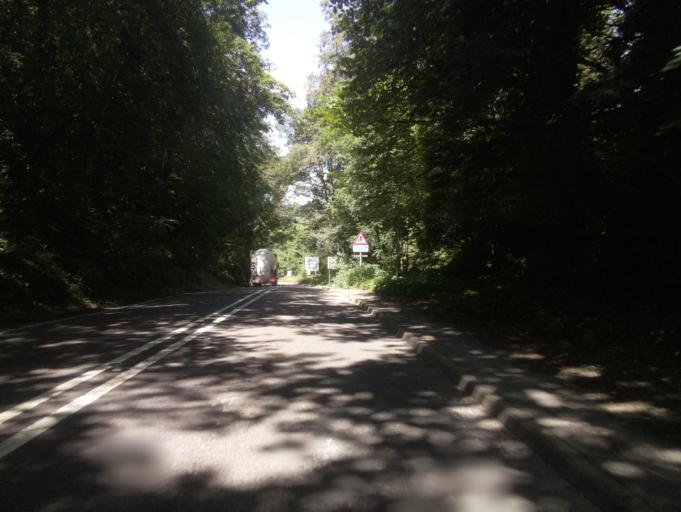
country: GB
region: England
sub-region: Derbyshire
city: Ashbourne
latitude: 53.0441
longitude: -1.7376
